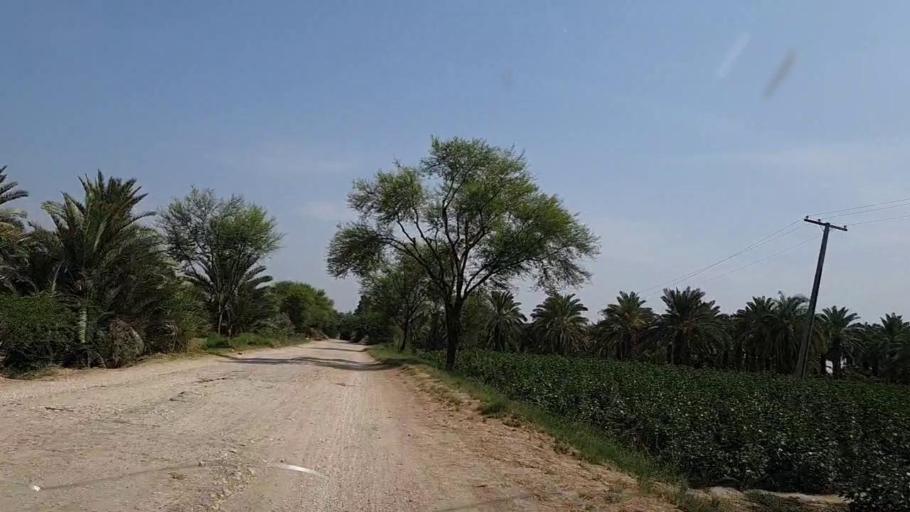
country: PK
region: Sindh
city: Khanpur
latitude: 27.7861
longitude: 69.3194
